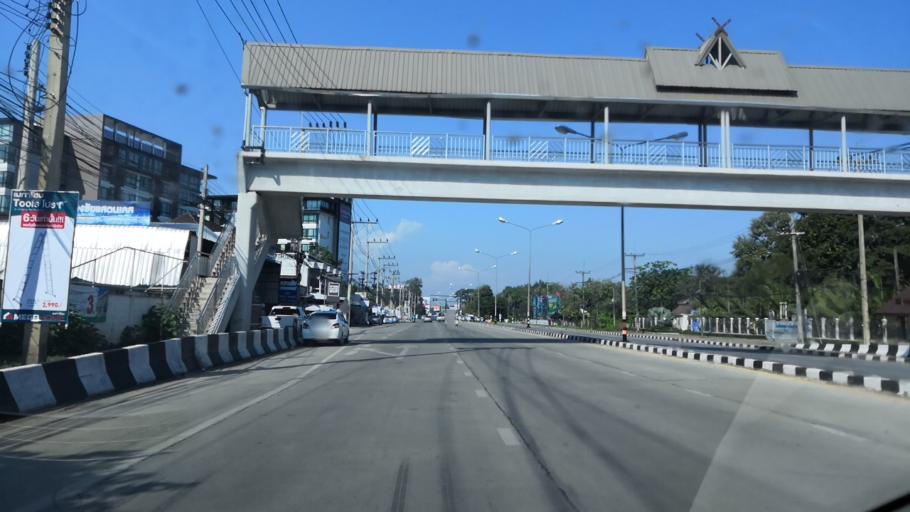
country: TH
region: Chiang Rai
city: Chiang Rai
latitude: 19.9351
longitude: 99.8449
